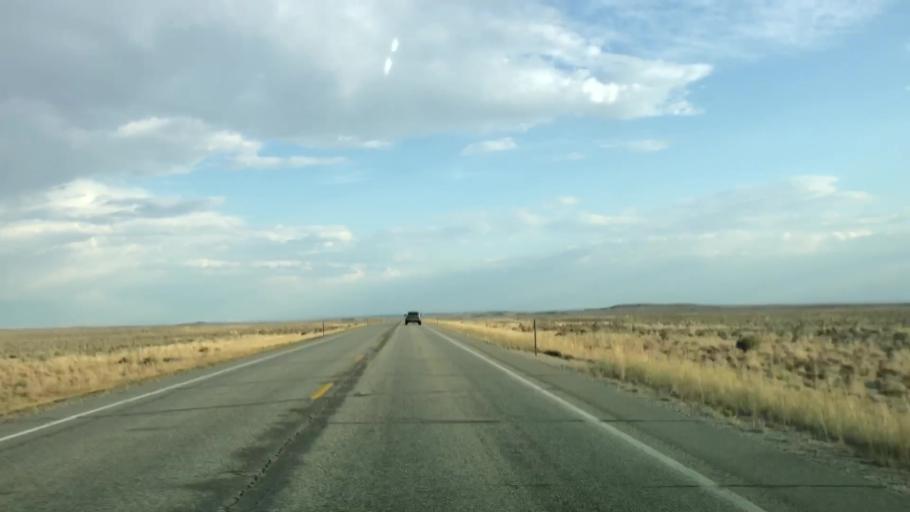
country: US
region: Wyoming
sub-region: Sublette County
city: Pinedale
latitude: 42.3908
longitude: -109.5405
